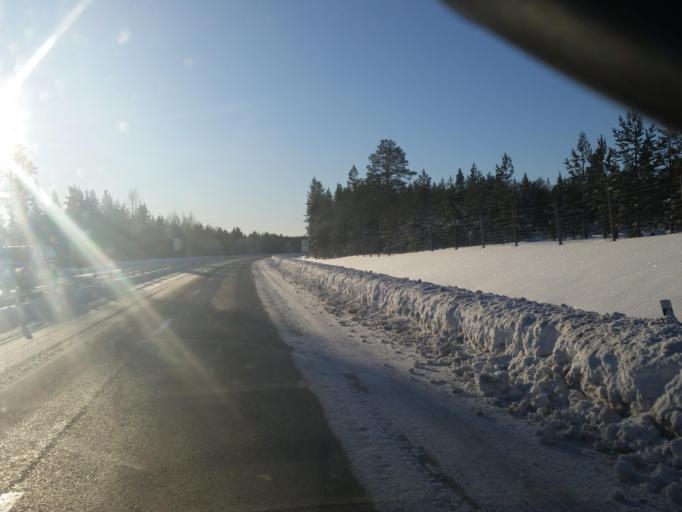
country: SE
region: Norrbotten
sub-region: Pitea Kommun
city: Pitea
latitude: 65.2191
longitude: 21.5186
